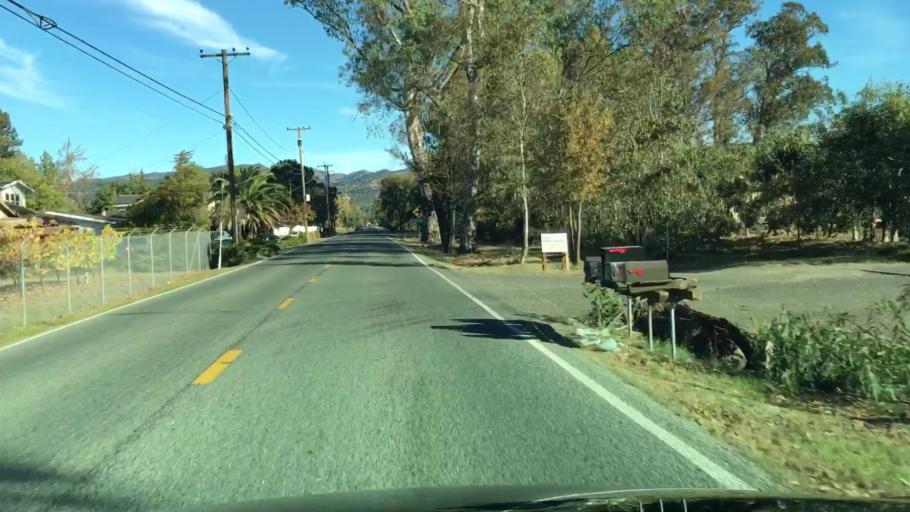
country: US
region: California
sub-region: Sonoma County
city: Sonoma
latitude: 38.2776
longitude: -122.4377
